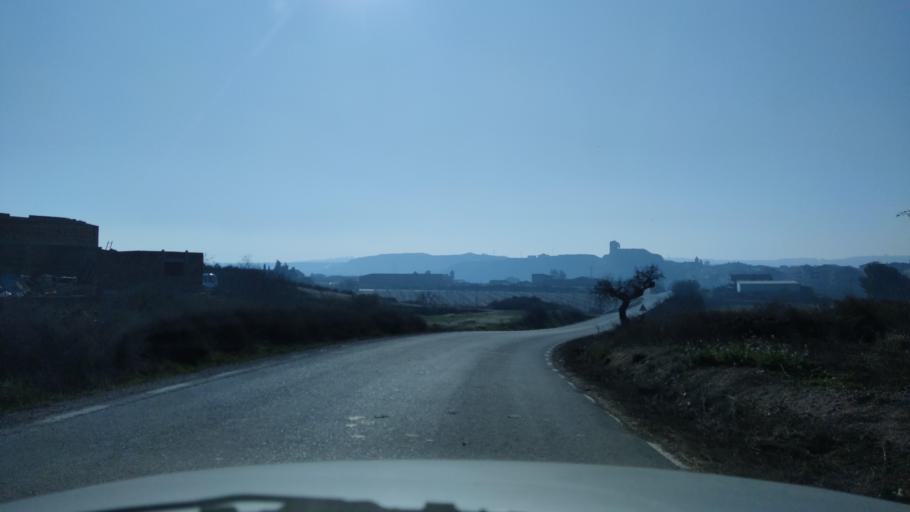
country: ES
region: Catalonia
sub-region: Provincia de Lleida
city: Torrebesses
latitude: 41.4639
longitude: 0.5655
